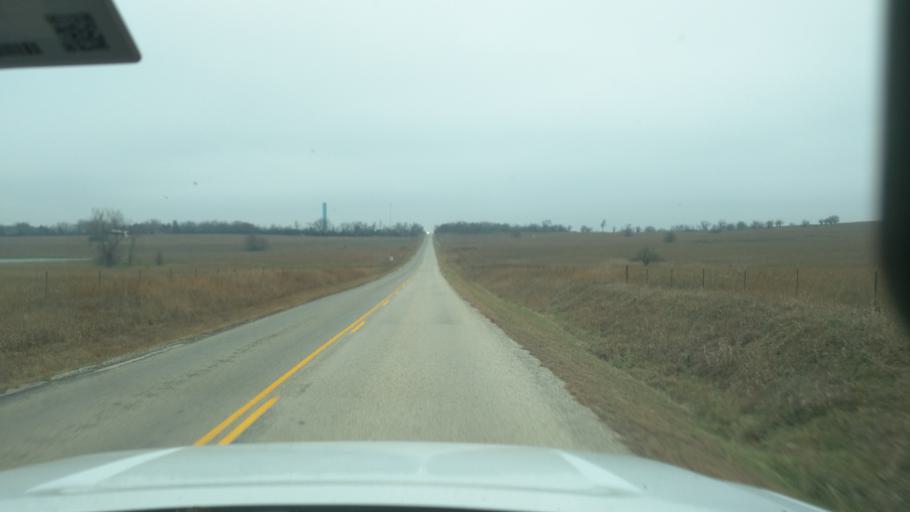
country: US
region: Kansas
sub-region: Morris County
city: Council Grove
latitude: 38.6511
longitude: -96.2615
